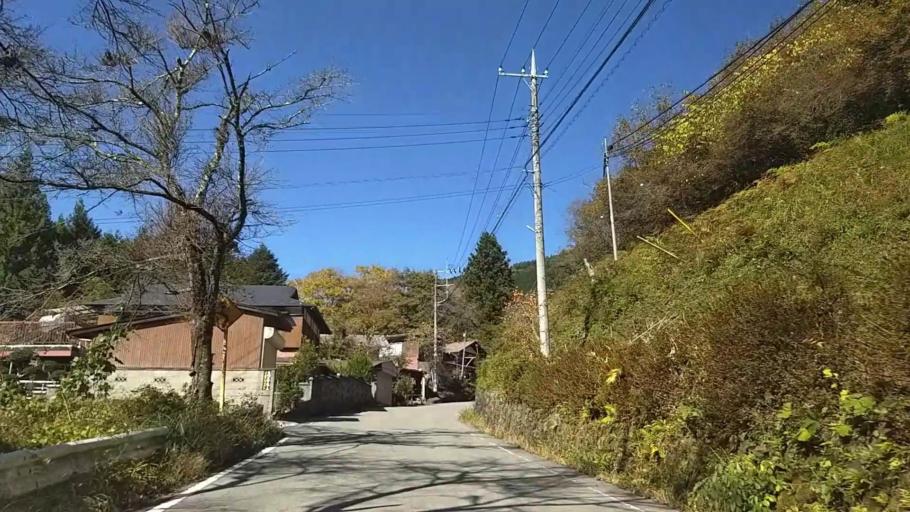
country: JP
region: Yamanashi
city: Uenohara
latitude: 35.7011
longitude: 139.0232
